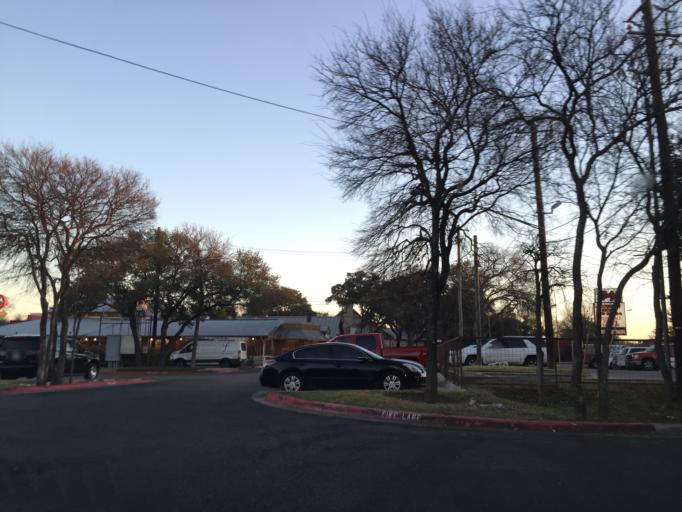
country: US
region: Texas
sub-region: Williamson County
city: Jollyville
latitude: 30.4147
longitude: -97.7474
